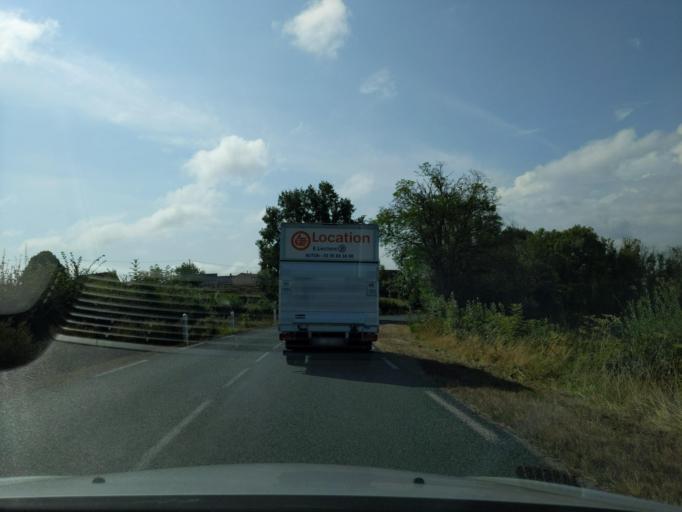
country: FR
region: Bourgogne
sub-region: Departement de Saone-et-Loire
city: Bourbon-Lancy
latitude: 46.6444
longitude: 3.7785
